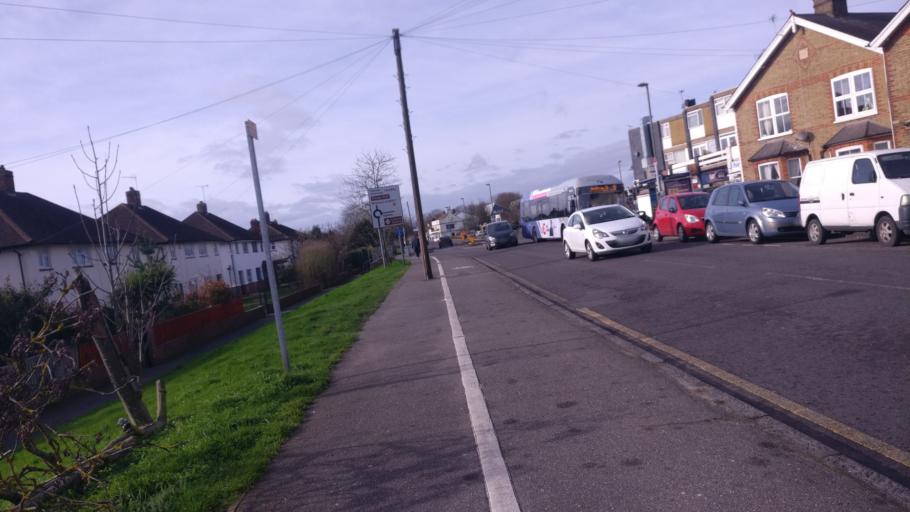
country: GB
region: England
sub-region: Surrey
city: Staines
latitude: 51.4271
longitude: -0.5269
